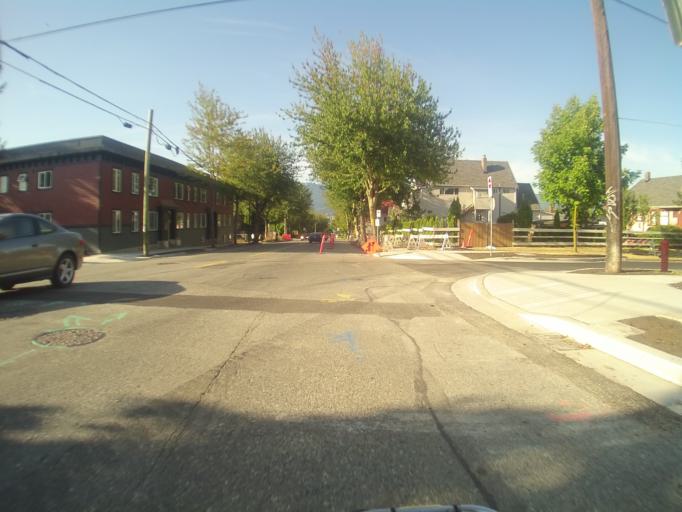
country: CA
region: British Columbia
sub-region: Fraser Valley Regional District
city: North Vancouver
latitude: 49.2775
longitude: -123.0655
